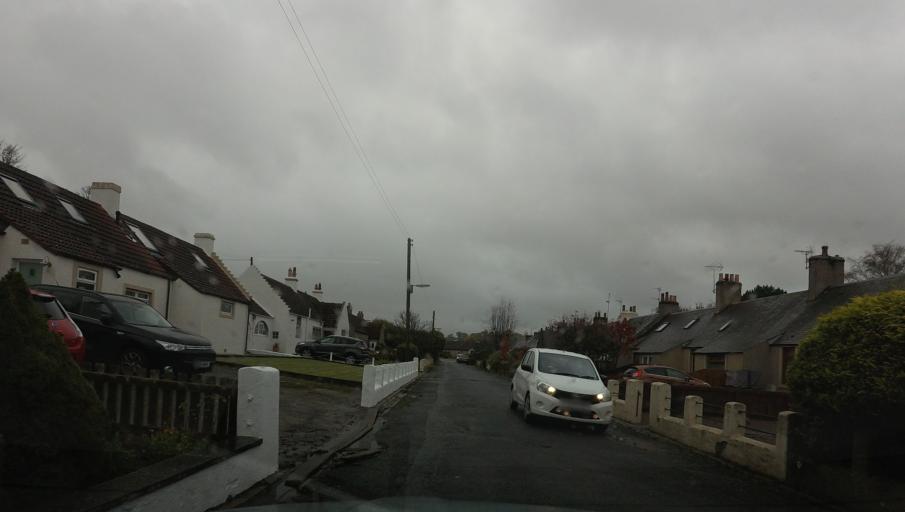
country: GB
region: Scotland
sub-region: Fife
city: East Wemyss
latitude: 56.1559
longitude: -3.0709
